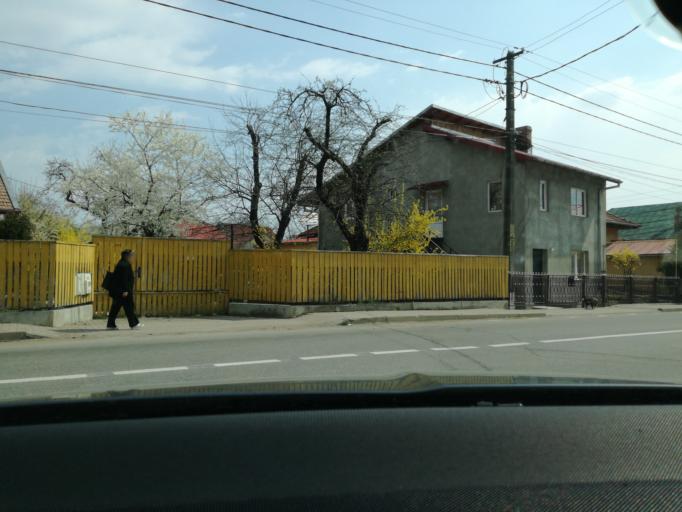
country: RO
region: Prahova
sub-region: Comuna Cornu
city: Cornu de Jos
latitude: 45.1593
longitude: 25.7022
